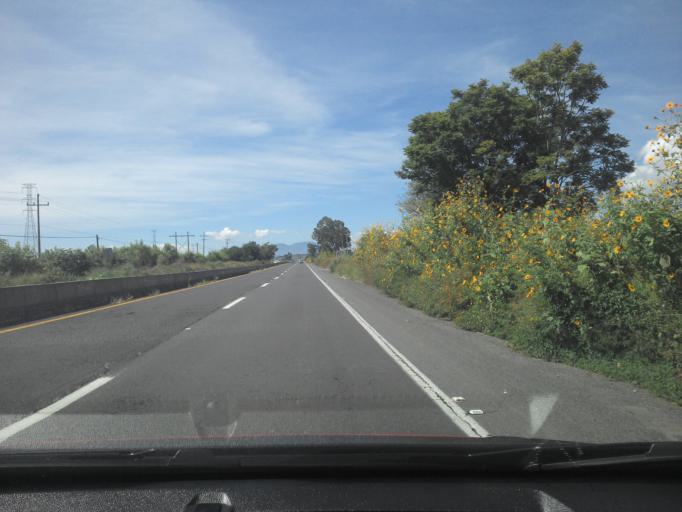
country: MX
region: Jalisco
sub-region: Tala
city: Los Ruisenores
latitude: 20.7107
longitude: -103.6639
